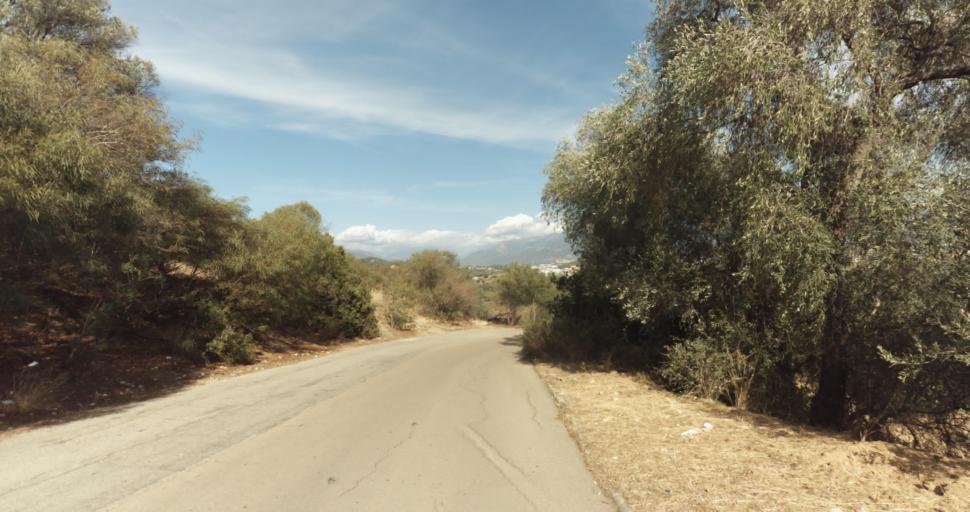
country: FR
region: Corsica
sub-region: Departement de la Corse-du-Sud
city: Ajaccio
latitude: 41.9344
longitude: 8.7180
